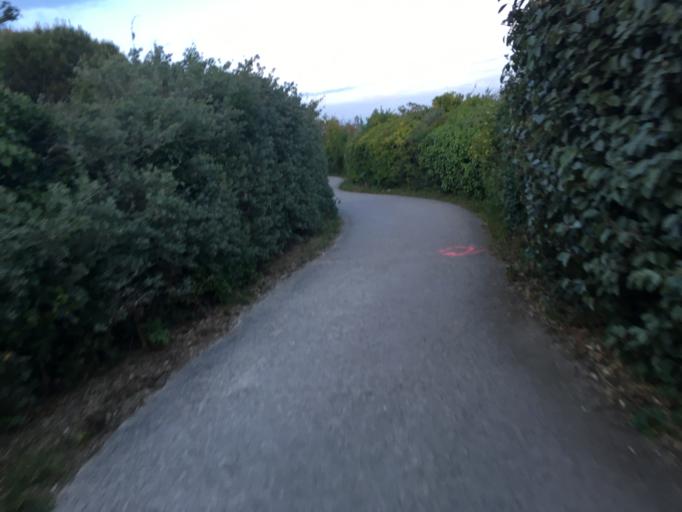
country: FR
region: Poitou-Charentes
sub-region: Departement de la Charente-Maritime
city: La Rochelle
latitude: 46.1488
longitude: -1.1961
